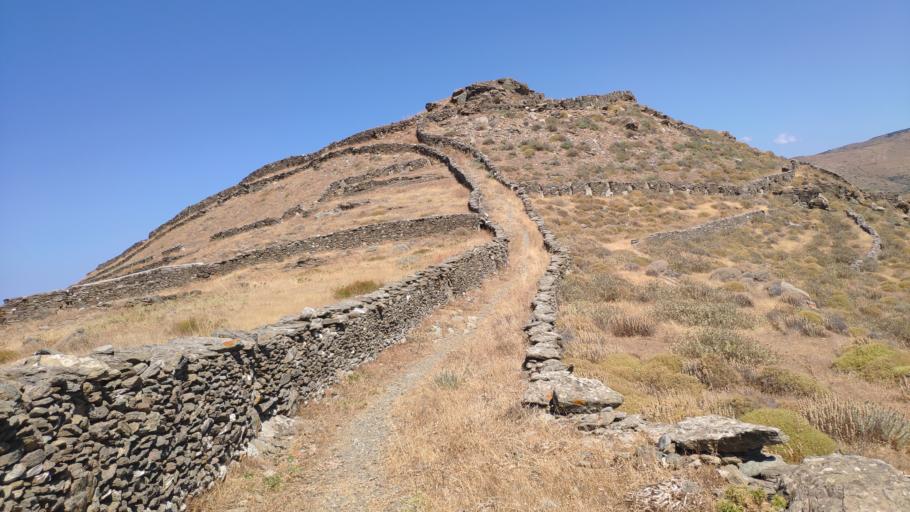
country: GR
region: South Aegean
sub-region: Nomos Kykladon
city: Kythnos
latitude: 37.4053
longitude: 24.3985
